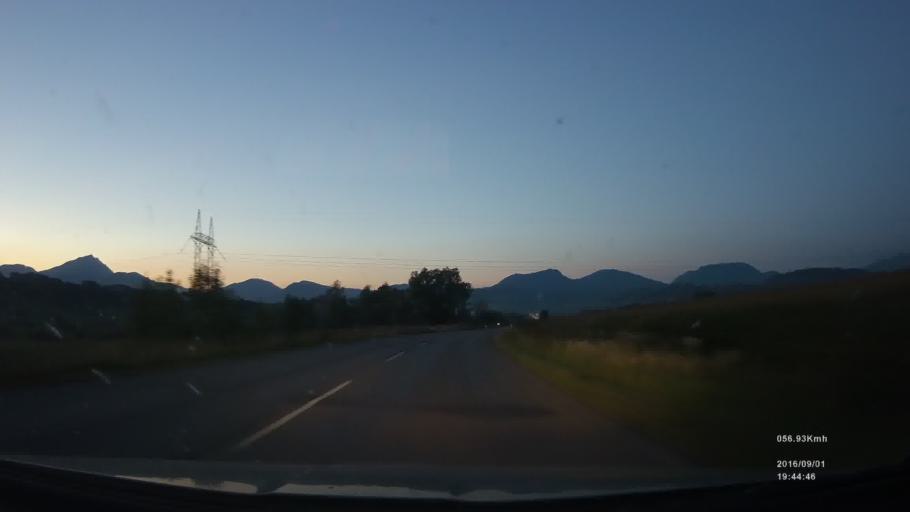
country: SK
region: Zilinsky
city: Ruzomberok
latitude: 49.0691
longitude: 19.4375
